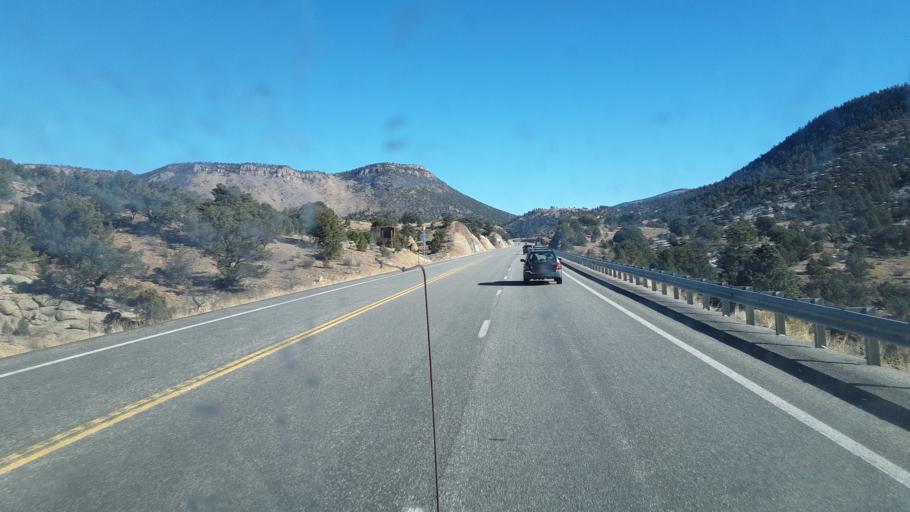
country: US
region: Colorado
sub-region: Chaffee County
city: Buena Vista
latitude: 38.8284
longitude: -106.0350
